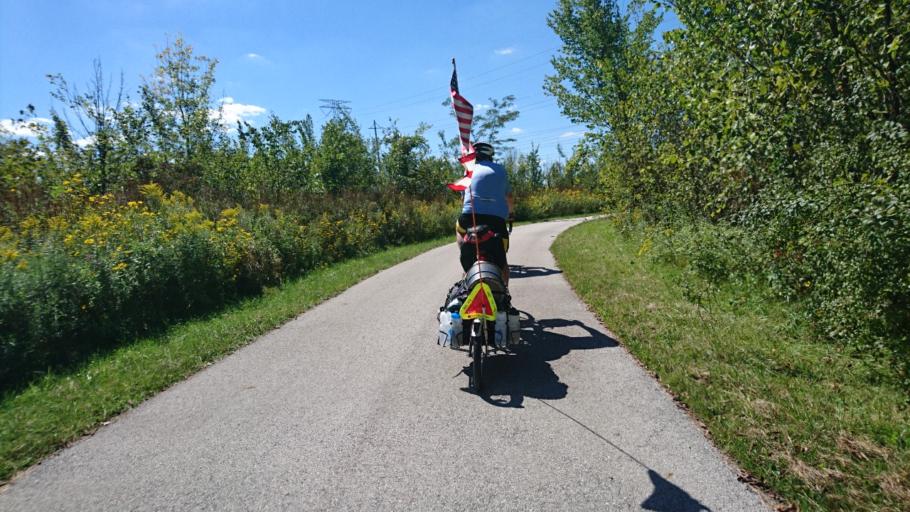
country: US
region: Illinois
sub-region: Cook County
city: Lansing
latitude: 41.5457
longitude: -87.5672
